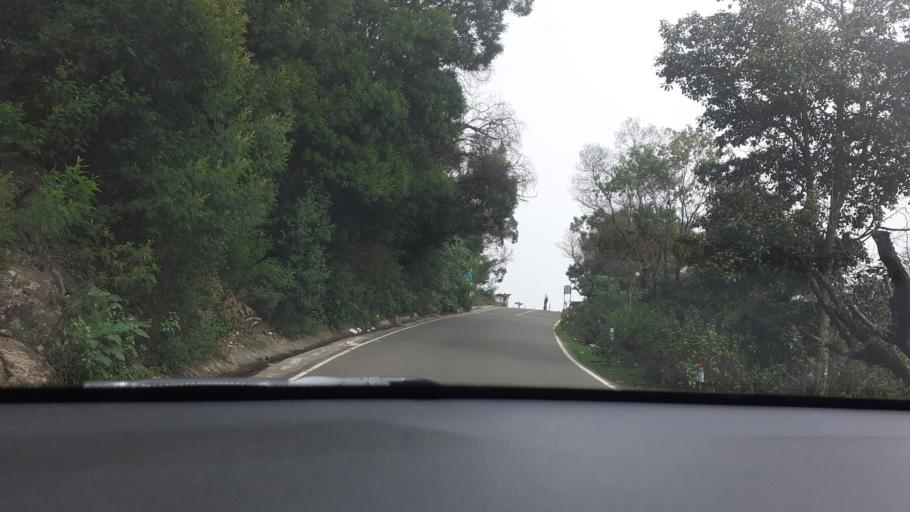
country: IN
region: Tamil Nadu
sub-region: Dindigul
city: Kodaikanal
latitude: 10.2476
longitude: 77.4169
